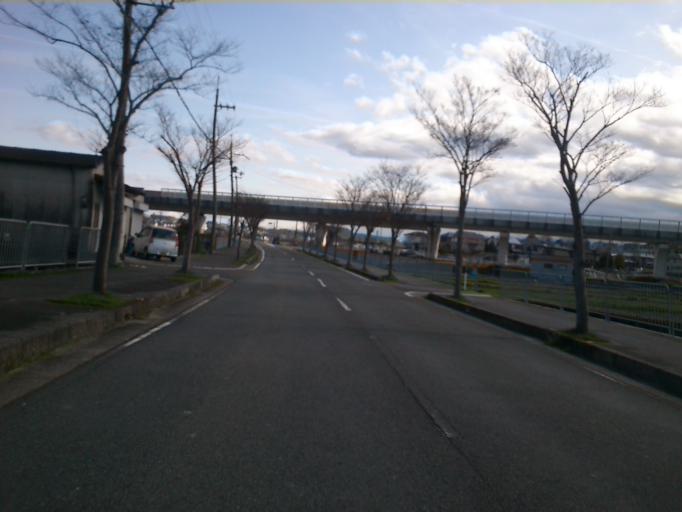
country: JP
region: Nara
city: Nara-shi
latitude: 34.7272
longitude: 135.8029
